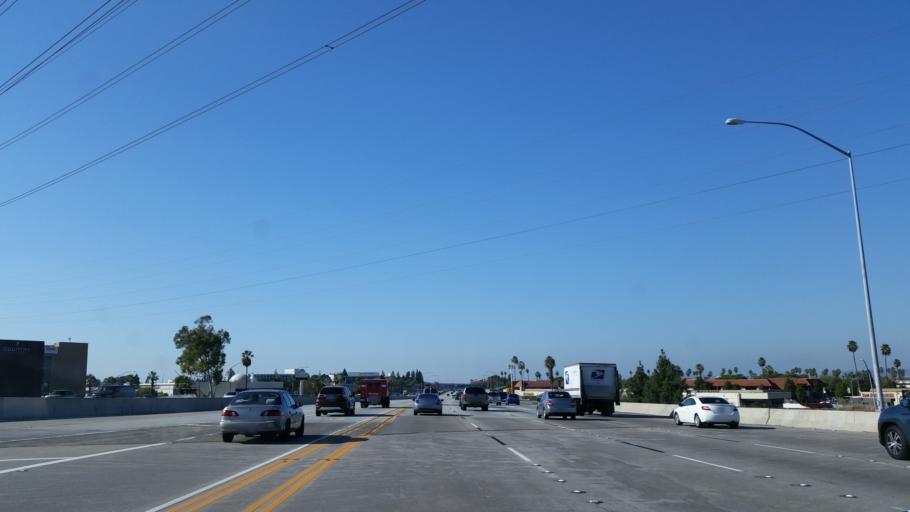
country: US
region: California
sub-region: Orange County
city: Anaheim
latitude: 33.8069
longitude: -117.9062
